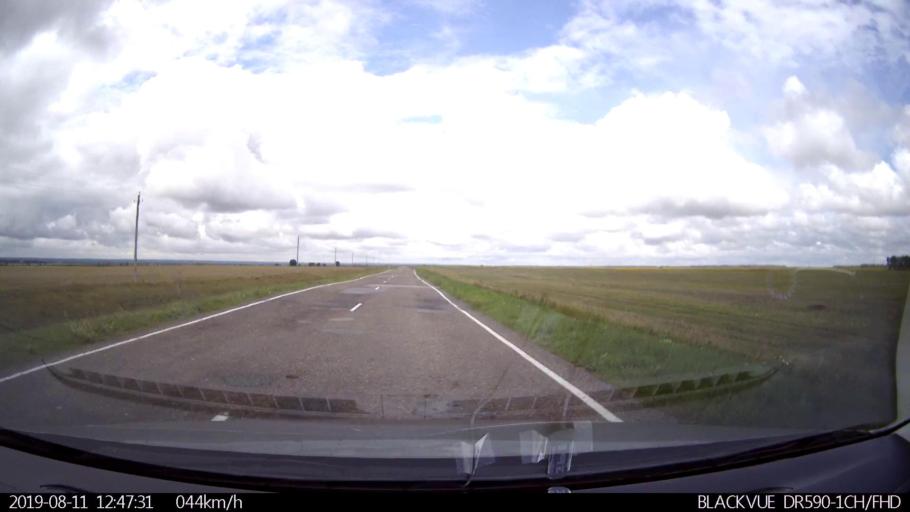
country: RU
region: Ulyanovsk
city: Ignatovka
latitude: 53.8697
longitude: 47.7081
